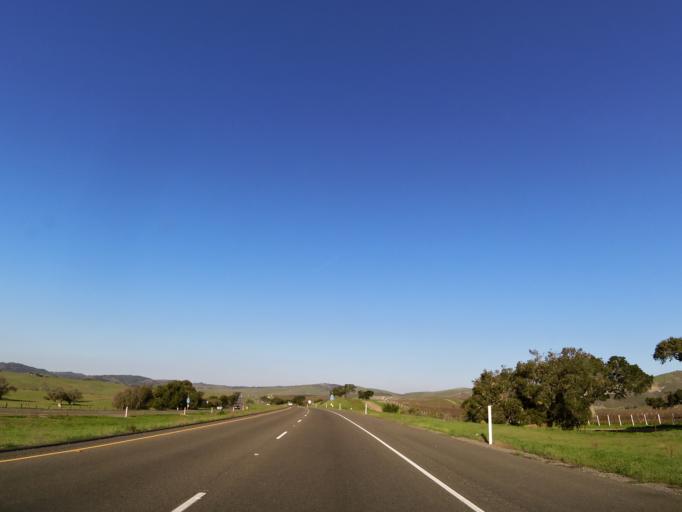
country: US
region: California
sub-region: Santa Barbara County
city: Los Alamos
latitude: 34.7839
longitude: -120.3184
